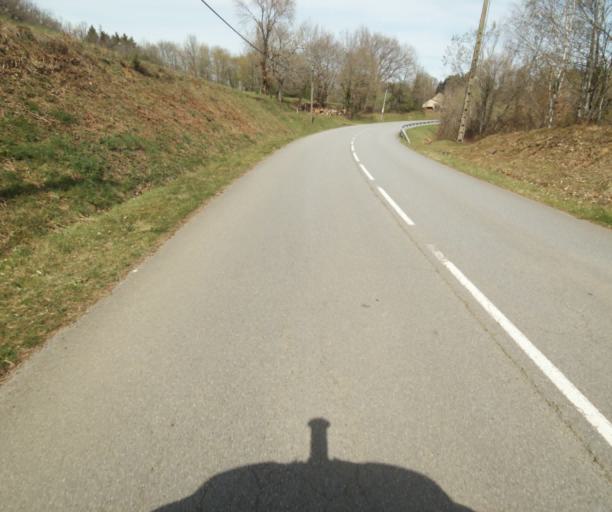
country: FR
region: Limousin
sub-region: Departement de la Correze
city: Correze
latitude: 45.3806
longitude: 1.8033
